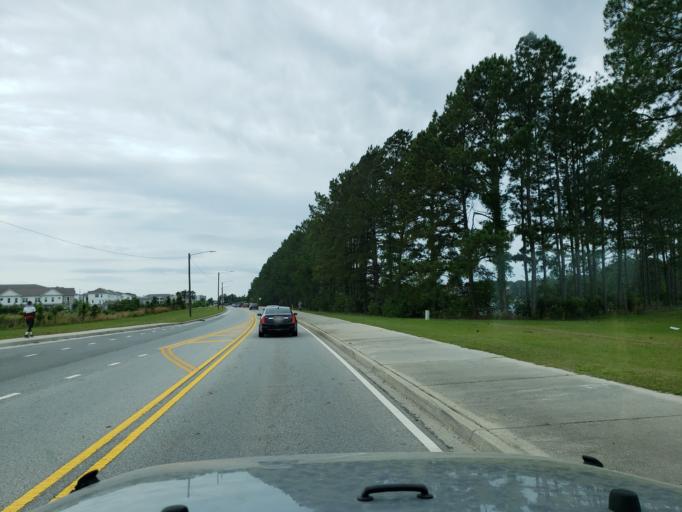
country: US
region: Georgia
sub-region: Chatham County
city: Pooler
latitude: 32.1530
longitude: -81.2430
